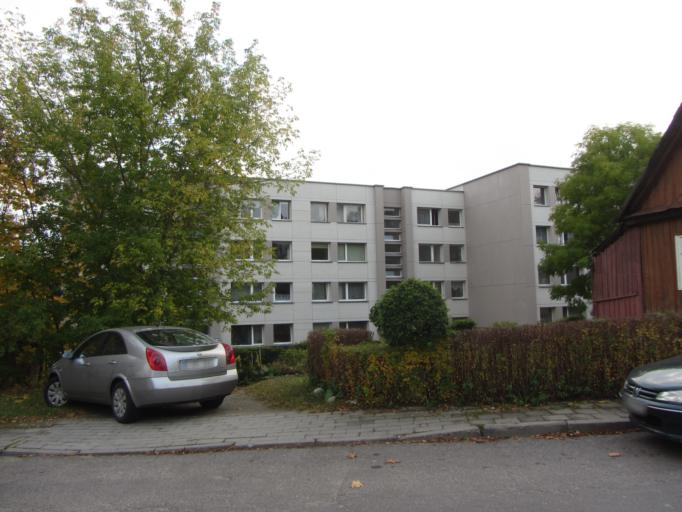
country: LT
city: Trakai
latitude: 54.6407
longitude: 24.9338
